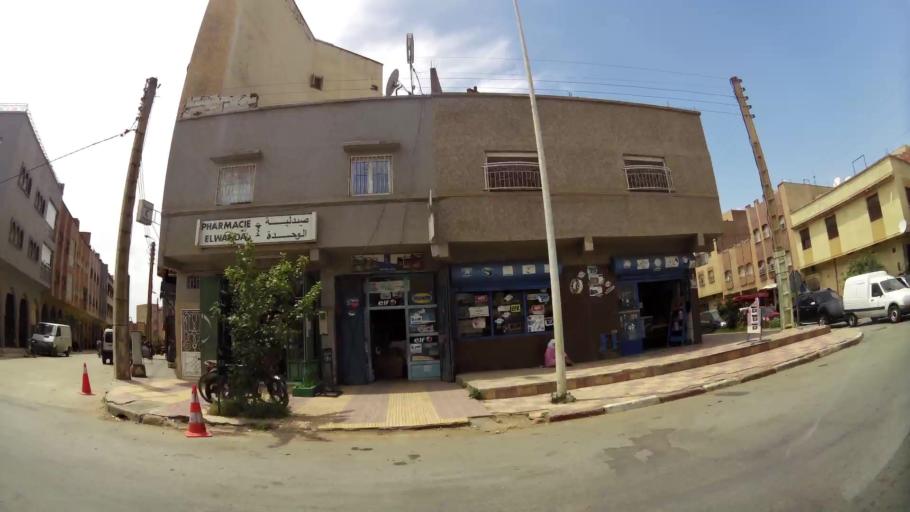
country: MA
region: Rabat-Sale-Zemmour-Zaer
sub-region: Khemisset
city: Khemisset
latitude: 33.8238
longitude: -6.0771
